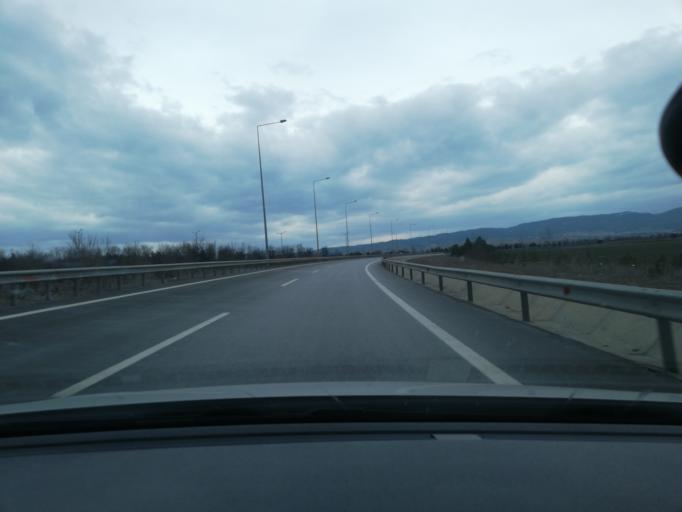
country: TR
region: Bolu
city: Gerede
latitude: 40.7380
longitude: 32.1964
